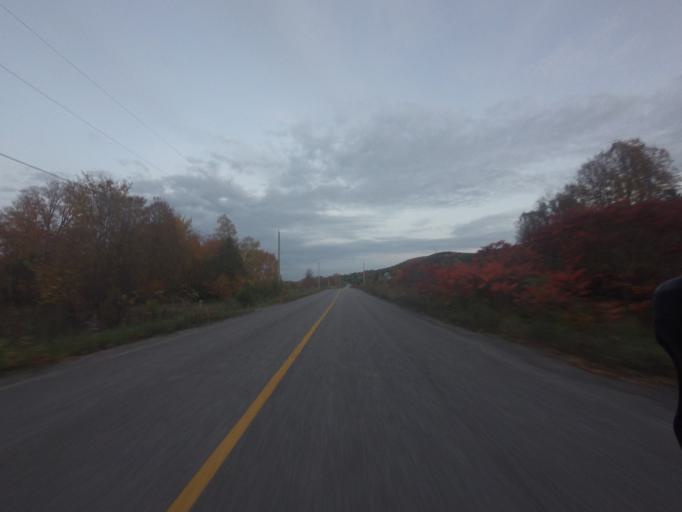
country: CA
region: Ontario
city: Renfrew
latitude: 45.3483
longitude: -76.9408
